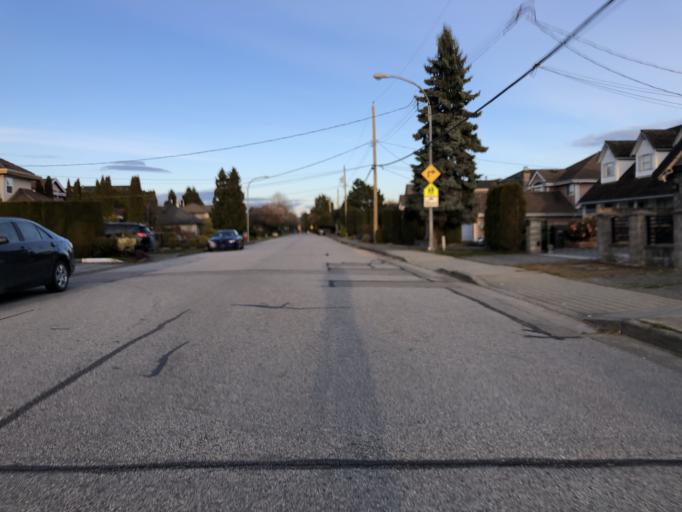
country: CA
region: British Columbia
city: Richmond
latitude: 49.1518
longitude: -123.1219
